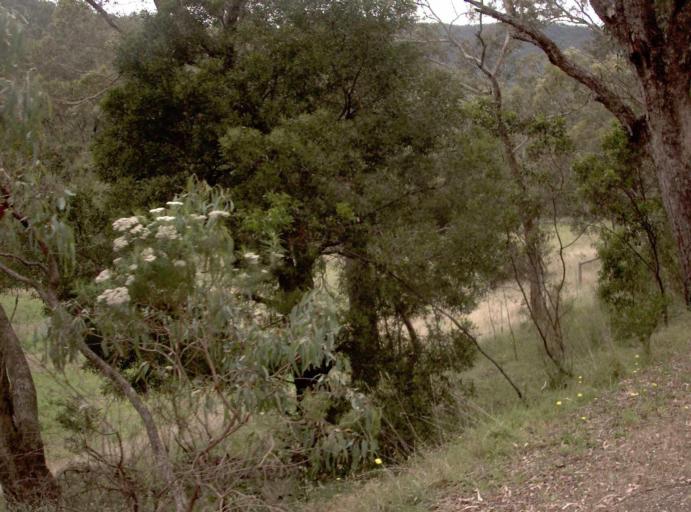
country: AU
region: Victoria
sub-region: East Gippsland
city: Bairnsdale
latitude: -37.5283
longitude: 147.2267
